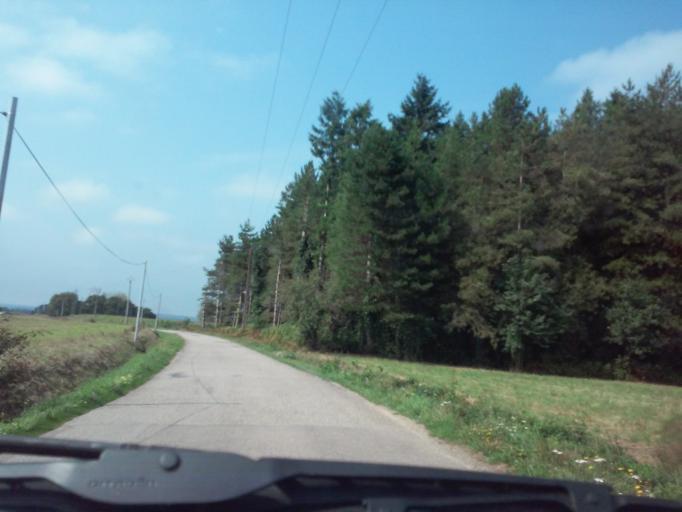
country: FR
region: Brittany
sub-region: Departement du Morbihan
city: Ploermel
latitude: 47.8986
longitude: -2.3875
